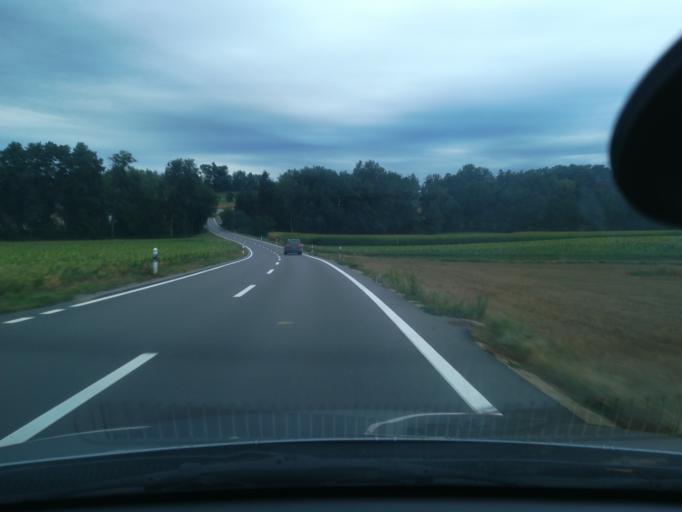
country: CH
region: Thurgau
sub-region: Frauenfeld District
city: Huttwilen
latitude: 47.6001
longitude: 8.8925
